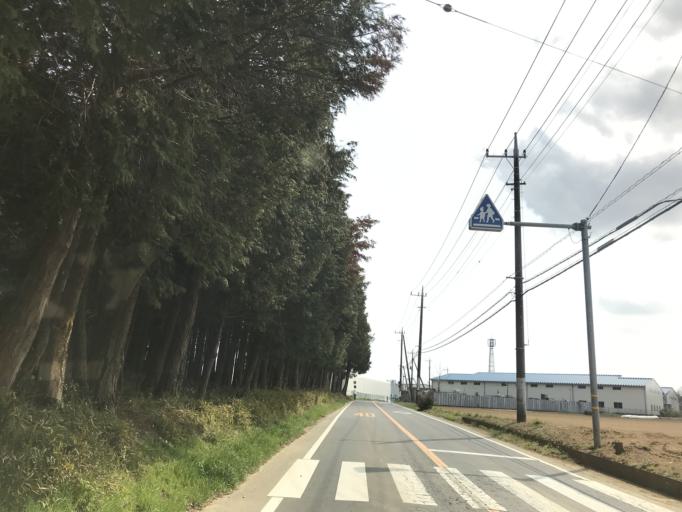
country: JP
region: Ibaraki
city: Ushiku
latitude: 36.0015
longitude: 140.0700
